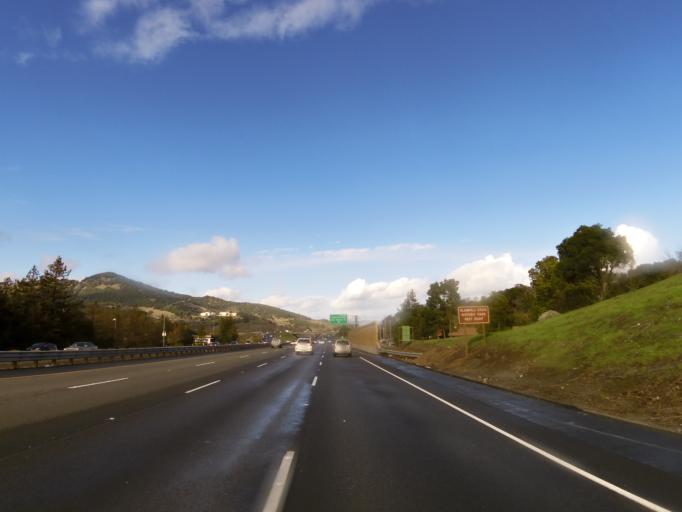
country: US
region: California
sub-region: Marin County
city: Novato
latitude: 38.1122
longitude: -122.5641
